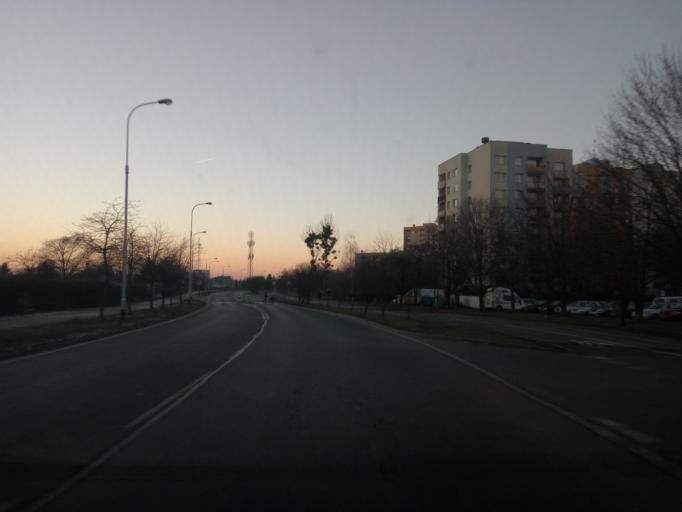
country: PL
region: Lower Silesian Voivodeship
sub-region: Powiat wroclawski
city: Bielany Wroclawskie
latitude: 51.1111
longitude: 16.9540
